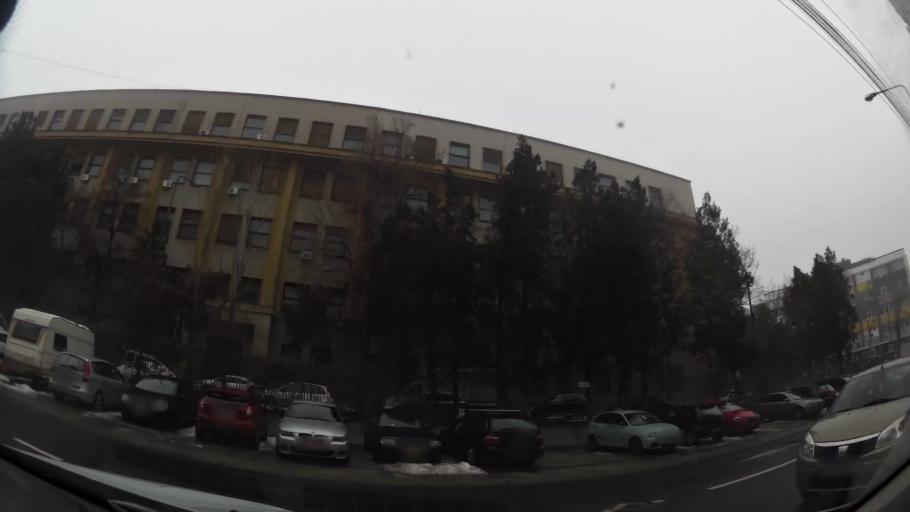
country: RO
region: Ilfov
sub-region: Comuna Chiajna
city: Rosu
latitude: 44.4557
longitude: 26.0414
